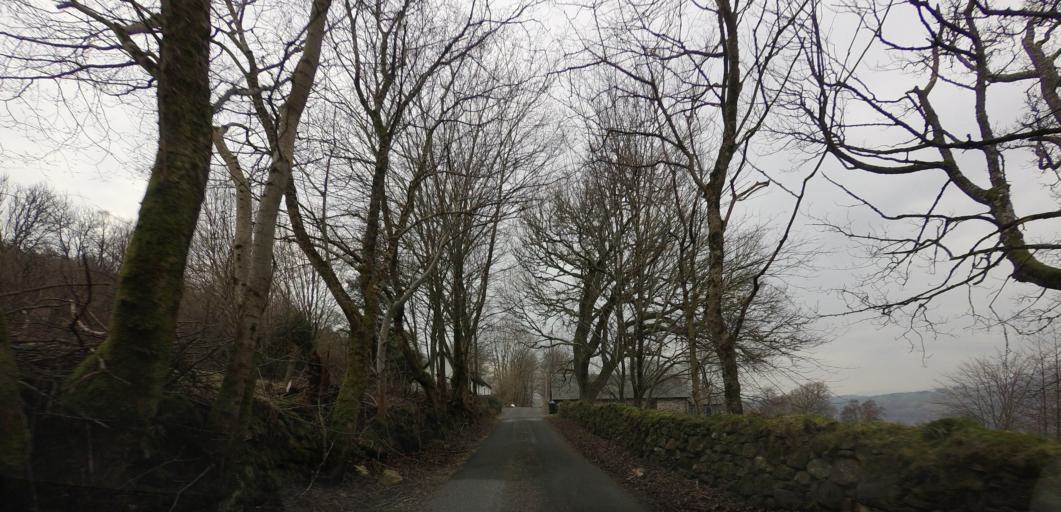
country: GB
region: Scotland
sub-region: Perth and Kinross
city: Comrie
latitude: 56.5375
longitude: -4.1042
